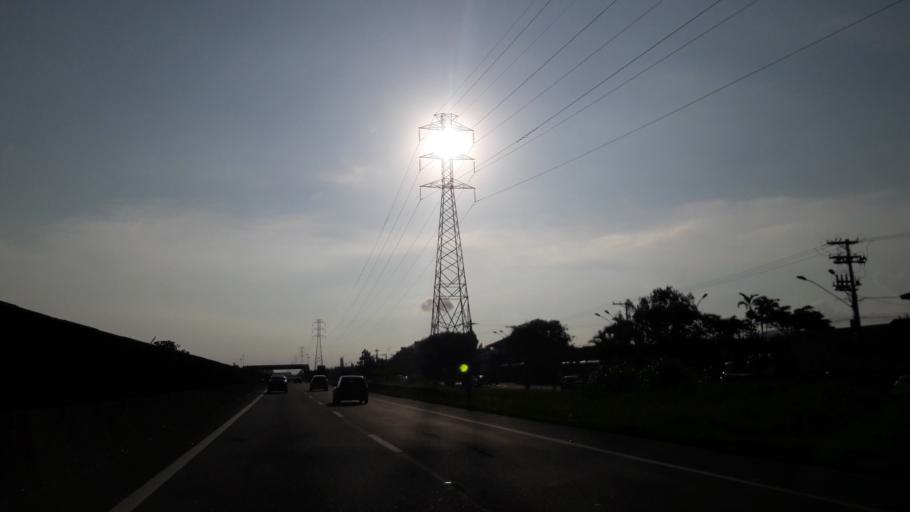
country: BR
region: Sao Paulo
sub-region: Mongagua
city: Mongagua
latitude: -24.1045
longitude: -46.6435
